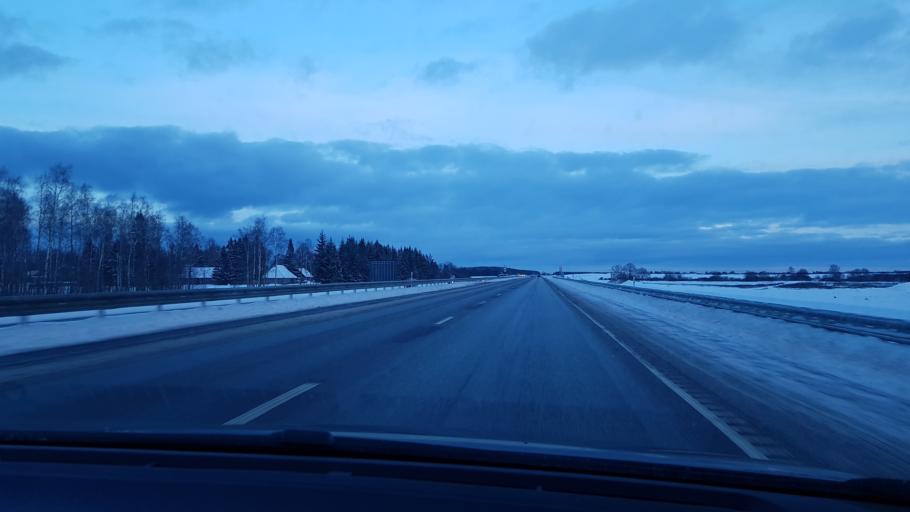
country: EE
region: Harju
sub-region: Maardu linn
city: Maardu
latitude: 59.4513
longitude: 25.0444
